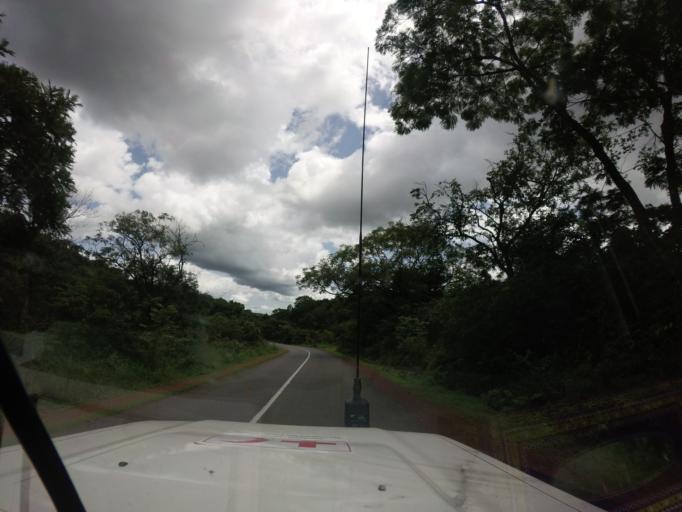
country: SL
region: Northern Province
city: Bindi
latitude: 10.1579
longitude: -11.5285
